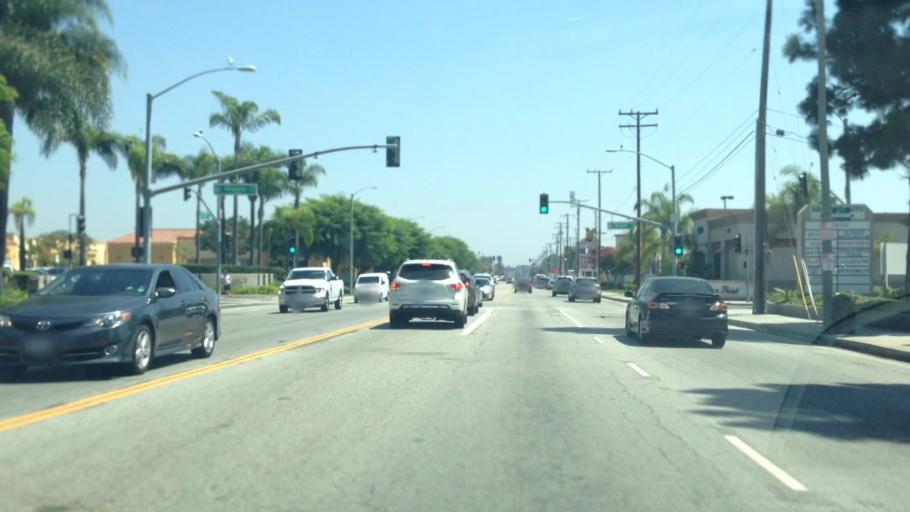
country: US
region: California
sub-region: Los Angeles County
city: West Carson
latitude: 33.8314
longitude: -118.3123
